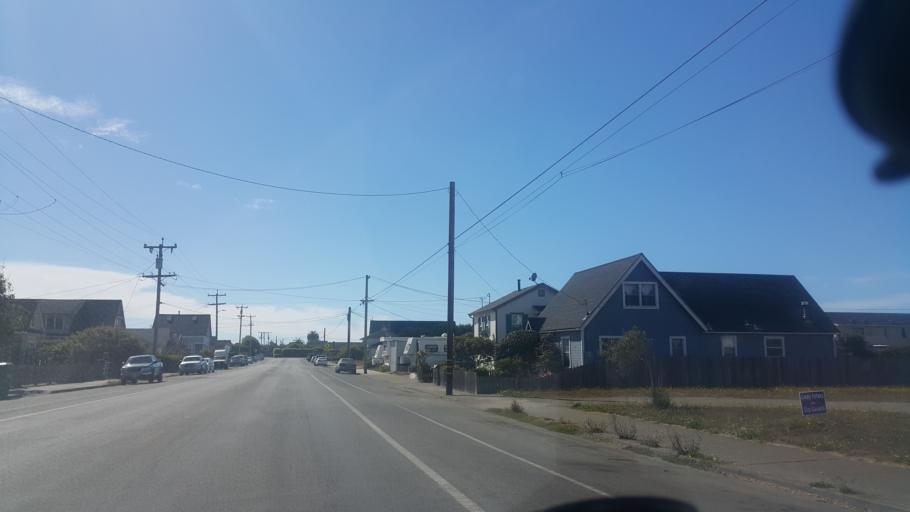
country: US
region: California
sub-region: Mendocino County
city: Fort Bragg
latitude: 39.4413
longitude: -123.7981
